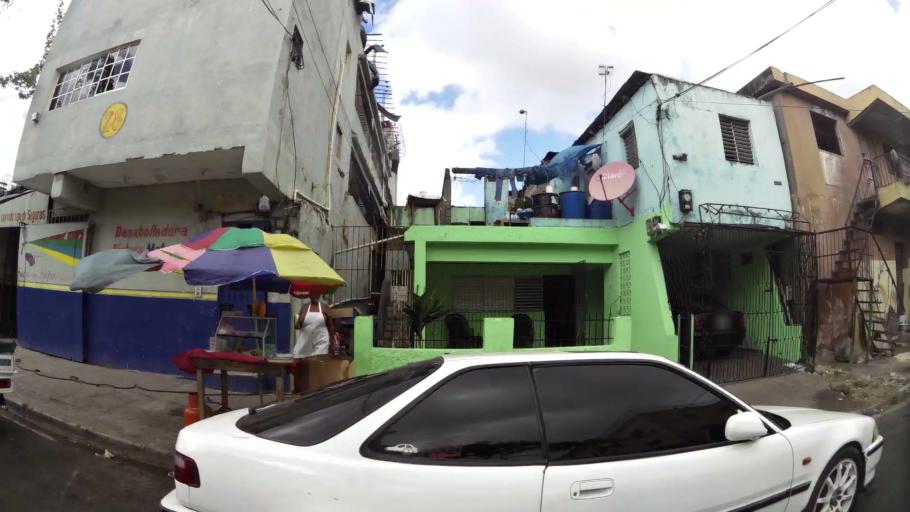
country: DO
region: Nacional
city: San Carlos
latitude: 18.4852
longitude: -69.8969
